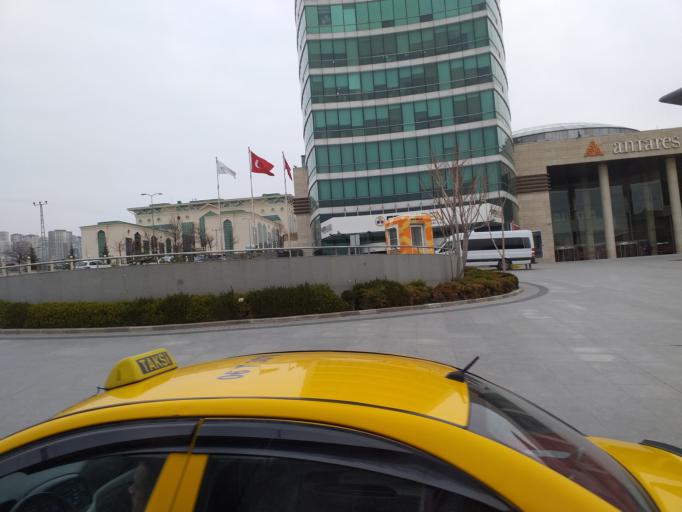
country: TR
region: Ankara
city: Ankara
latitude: 39.9691
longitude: 32.8193
